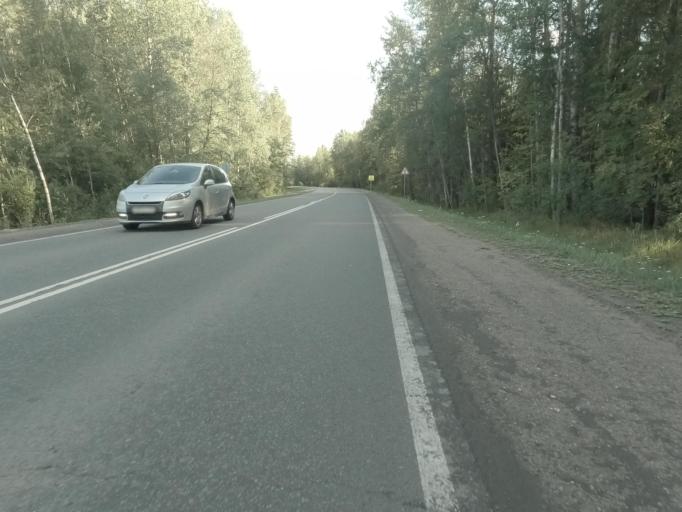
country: RU
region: Leningrad
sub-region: Volosovskiy Rayon
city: Shlissel'burg
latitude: 59.9404
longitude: 30.9826
